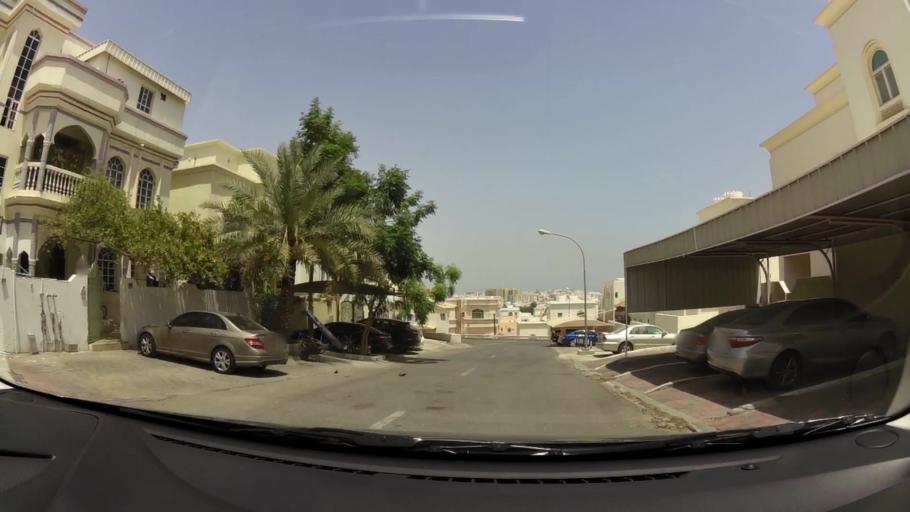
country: OM
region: Muhafazat Masqat
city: Bawshar
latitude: 23.5848
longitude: 58.4401
